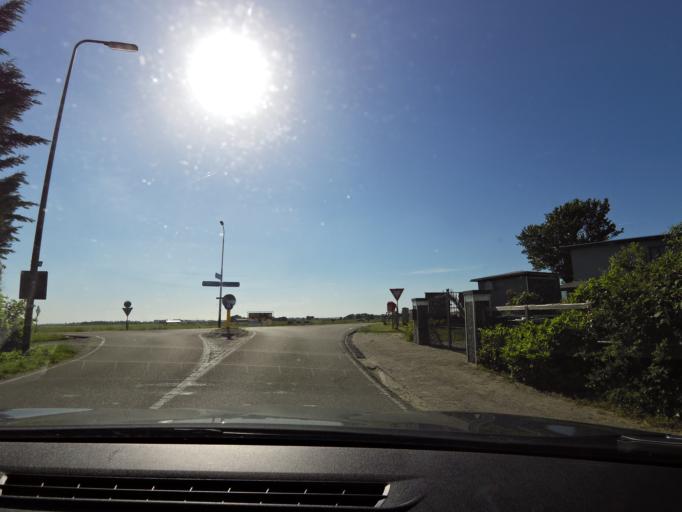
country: NL
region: South Holland
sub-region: Gemeente Hellevoetsluis
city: Nieuwenhoorn
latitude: 51.8671
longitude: 4.1607
